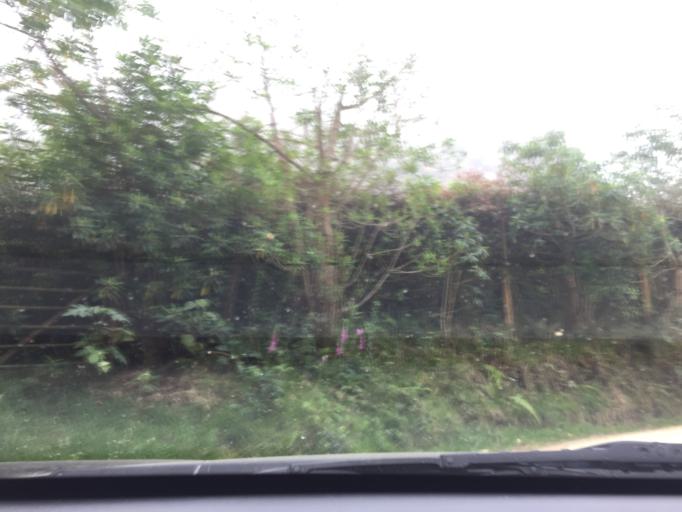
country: CO
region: Cundinamarca
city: Bojaca
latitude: 4.7026
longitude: -74.3625
